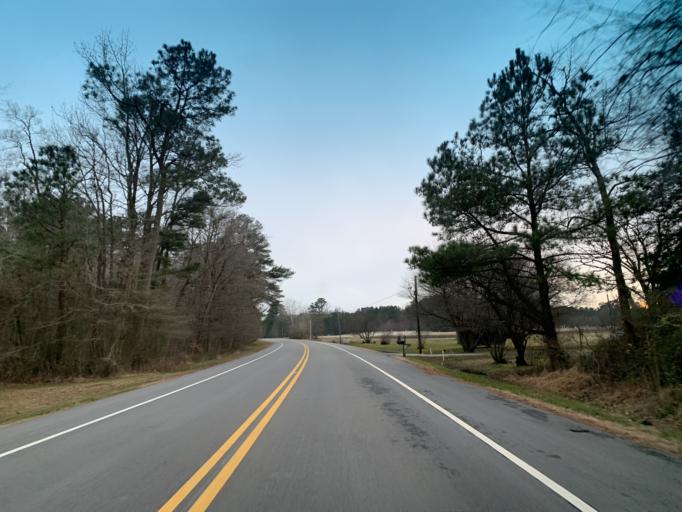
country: US
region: Maryland
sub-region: Worcester County
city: Pocomoke City
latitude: 38.0787
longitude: -75.5444
